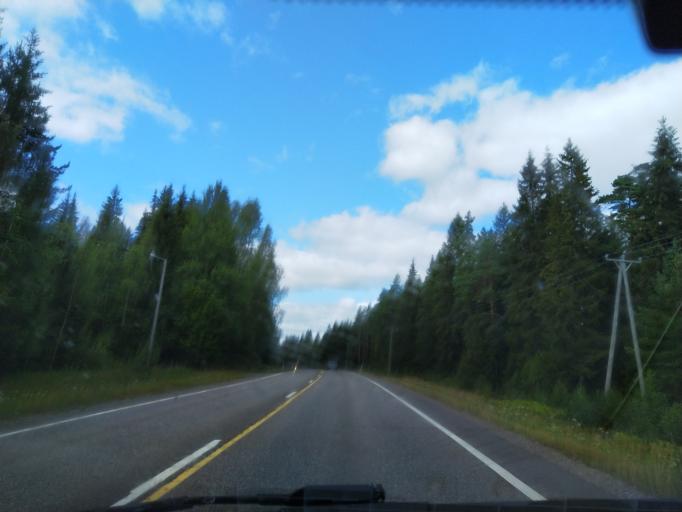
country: FI
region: Haeme
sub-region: Haemeenlinna
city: Renko
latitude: 60.7590
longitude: 24.2935
